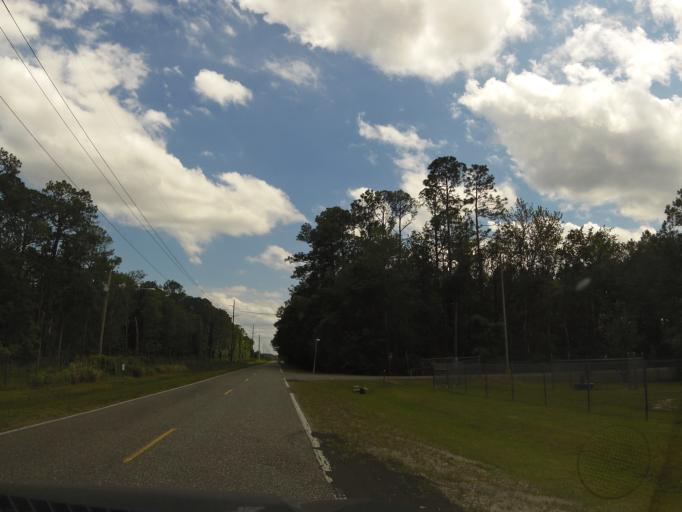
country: US
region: Florida
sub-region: Clay County
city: Green Cove Springs
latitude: 29.9766
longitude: -81.7394
